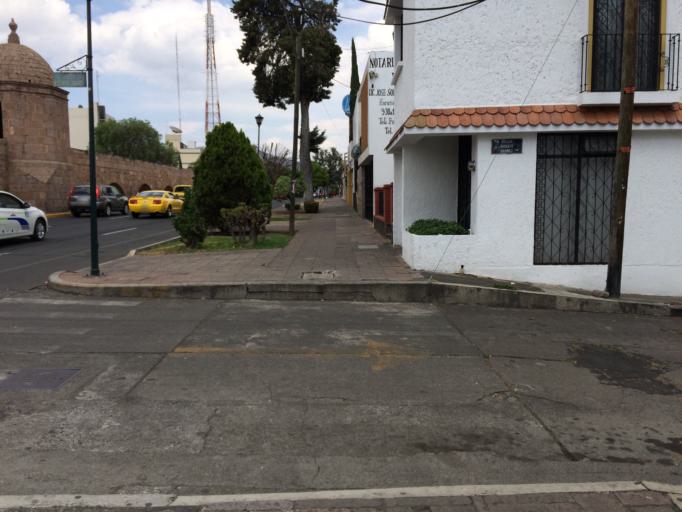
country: MX
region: Michoacan
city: Morelia
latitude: 19.6978
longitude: -101.1746
